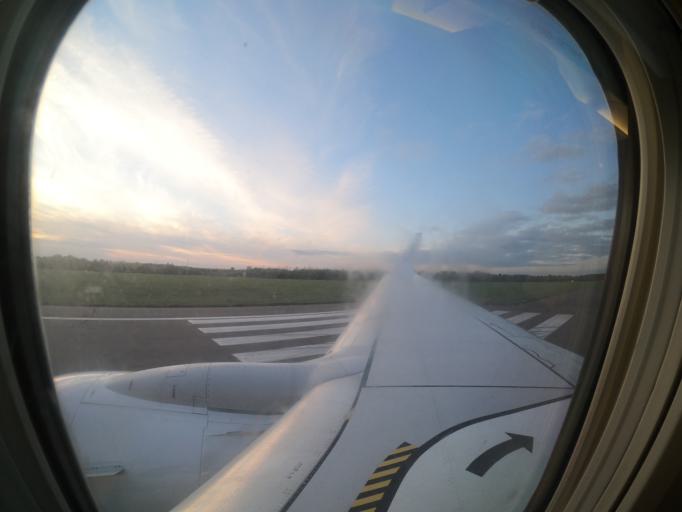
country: GB
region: England
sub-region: Essex
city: Elsenham
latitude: 51.8949
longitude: 0.2498
